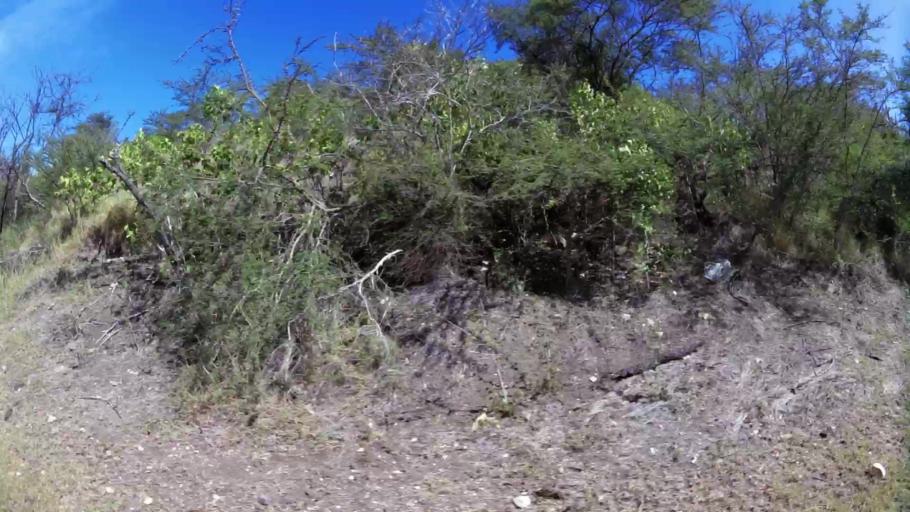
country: AG
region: Saint Paul
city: Falmouth
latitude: 17.0200
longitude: -61.7409
